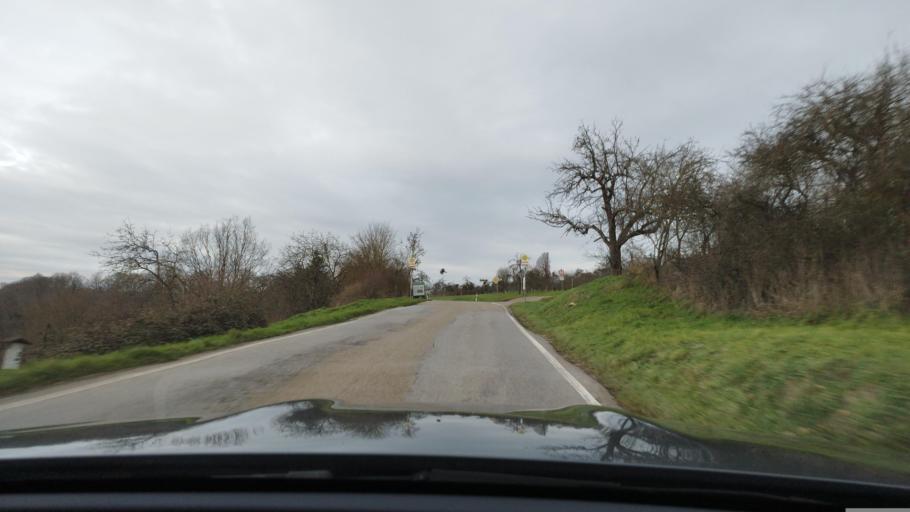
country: DE
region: Baden-Wuerttemberg
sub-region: Regierungsbezirk Stuttgart
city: Burgstetten
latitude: 48.9337
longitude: 9.3637
